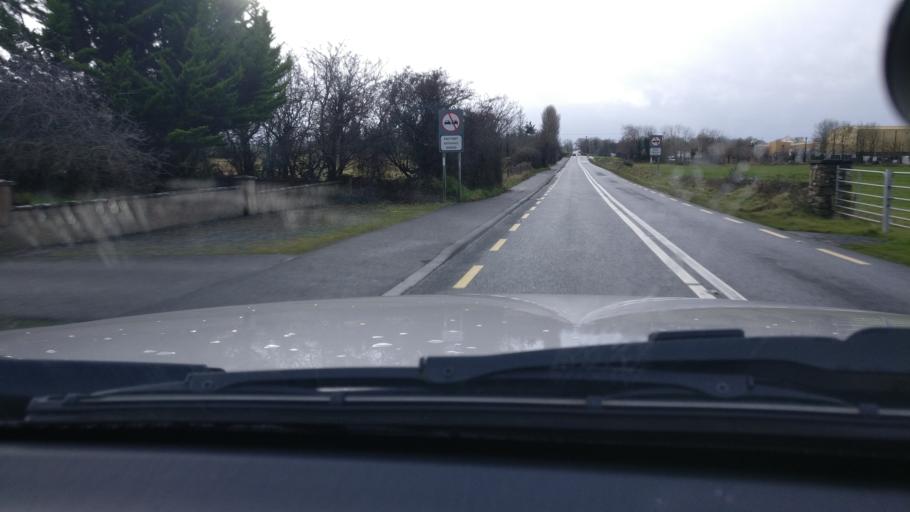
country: IE
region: Leinster
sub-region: An Longfort
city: Ballymahon
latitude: 53.5550
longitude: -7.7697
